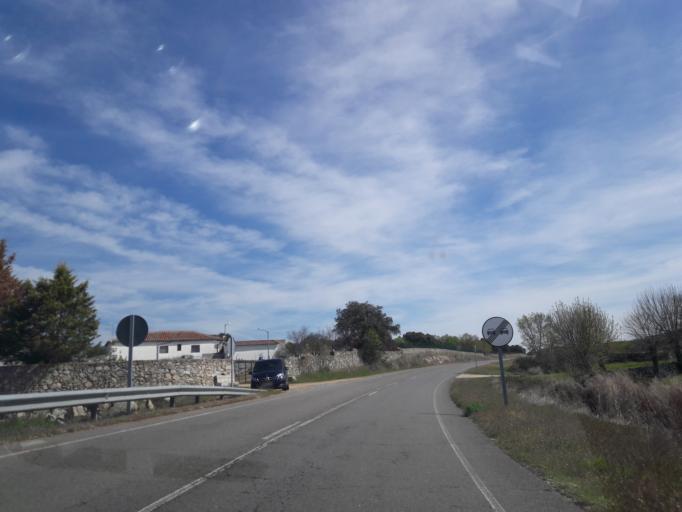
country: ES
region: Castille and Leon
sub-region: Provincia de Salamanca
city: Ledrada
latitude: 40.4898
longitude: -5.7213
